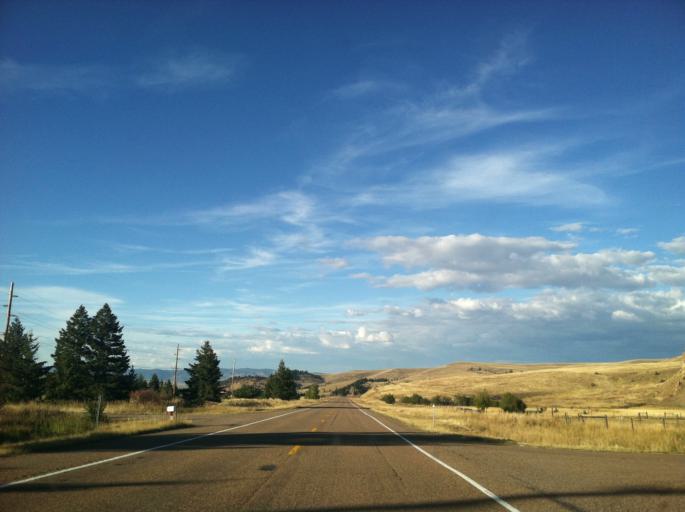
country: US
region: Montana
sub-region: Granite County
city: Philipsburg
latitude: 46.4832
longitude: -113.2334
